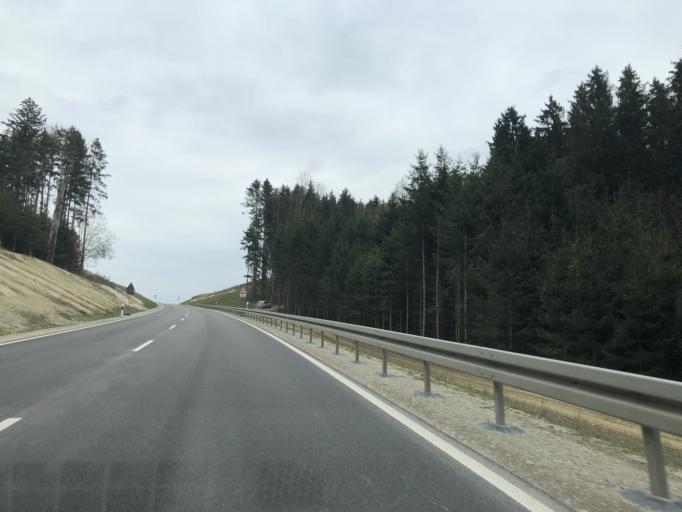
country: DE
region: Bavaria
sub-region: Upper Bavaria
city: Zolling
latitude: 48.4339
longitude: 11.7650
